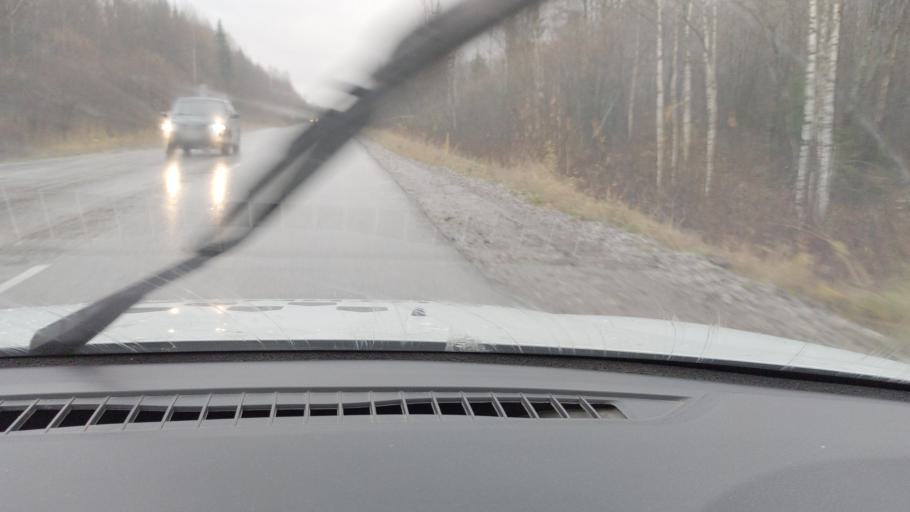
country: RU
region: Perm
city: Novyye Lyady
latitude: 58.0307
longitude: 56.6182
